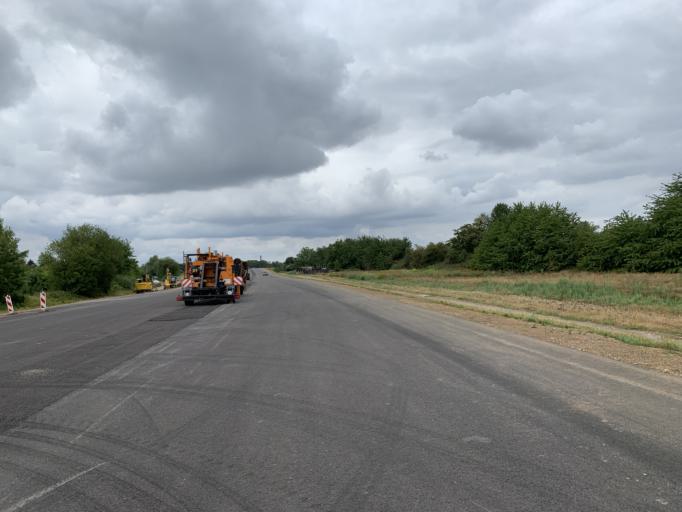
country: DE
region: North Rhine-Westphalia
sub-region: Regierungsbezirk Koln
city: Dueren
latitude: 50.8186
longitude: 6.4997
